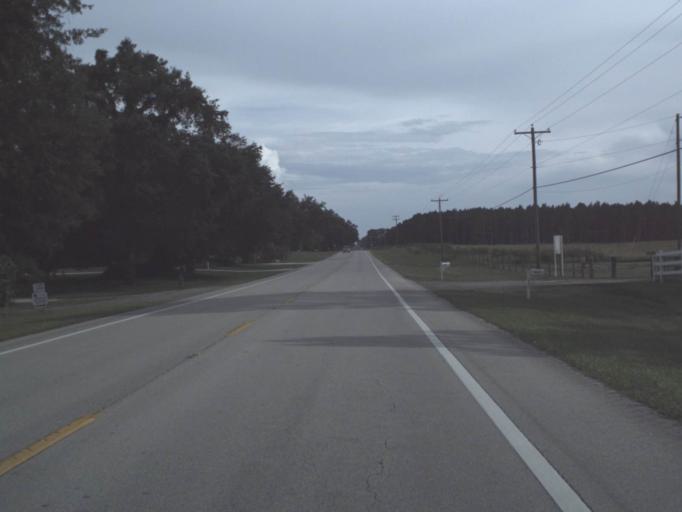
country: US
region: Florida
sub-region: Gilchrist County
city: Trenton
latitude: 29.5883
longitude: -82.8233
